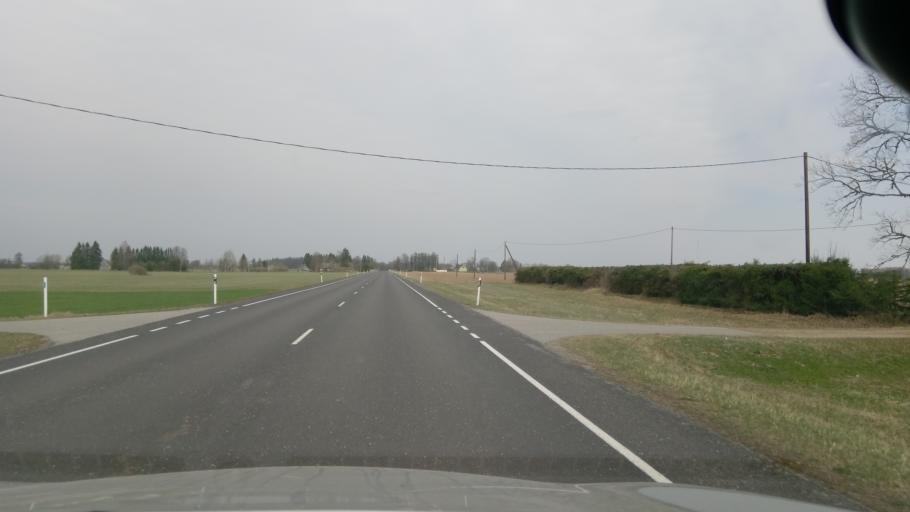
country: EE
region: Viljandimaa
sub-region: Vohma linn
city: Vohma
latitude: 58.6817
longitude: 25.6112
